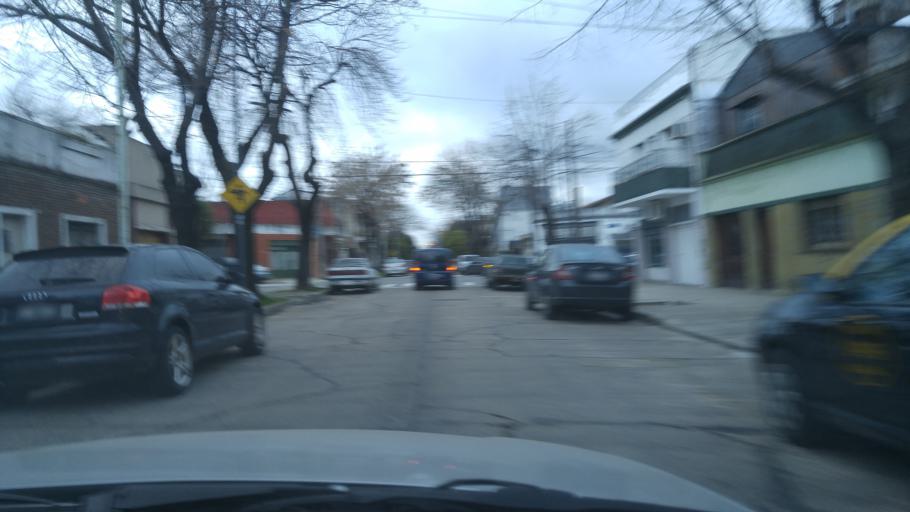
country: AR
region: Buenos Aires
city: Caseros
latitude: -34.6195
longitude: -58.5255
